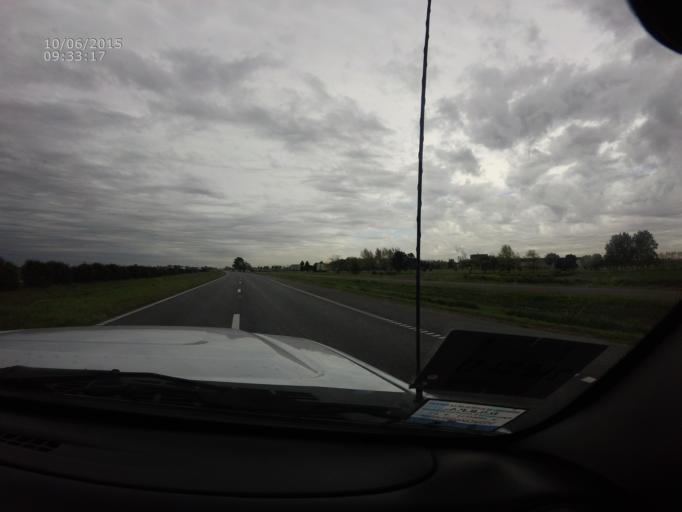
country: AR
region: Buenos Aires
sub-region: Partido de Zarate
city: Zarate
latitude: -34.1205
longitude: -59.0948
